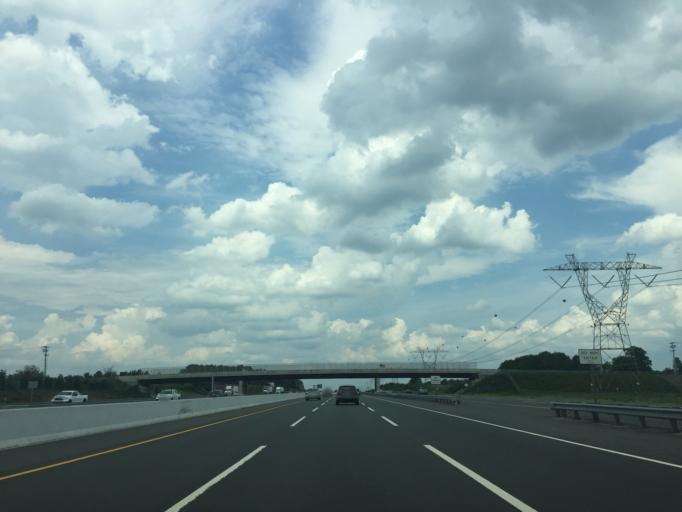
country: US
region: New Jersey
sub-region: Monmouth County
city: Allentown
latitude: 40.2079
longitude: -74.5800
